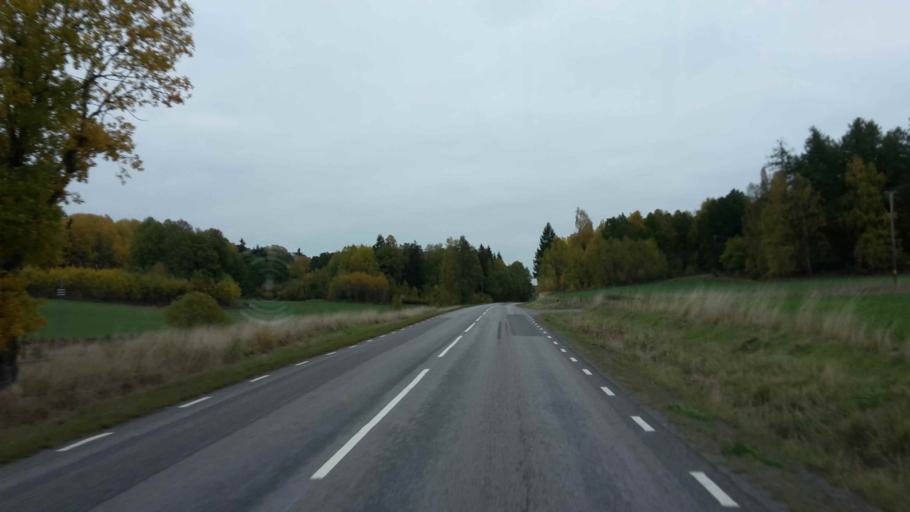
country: SE
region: OEstergoetland
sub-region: Atvidabergs Kommun
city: Atvidaberg
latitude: 58.1546
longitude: 16.1613
